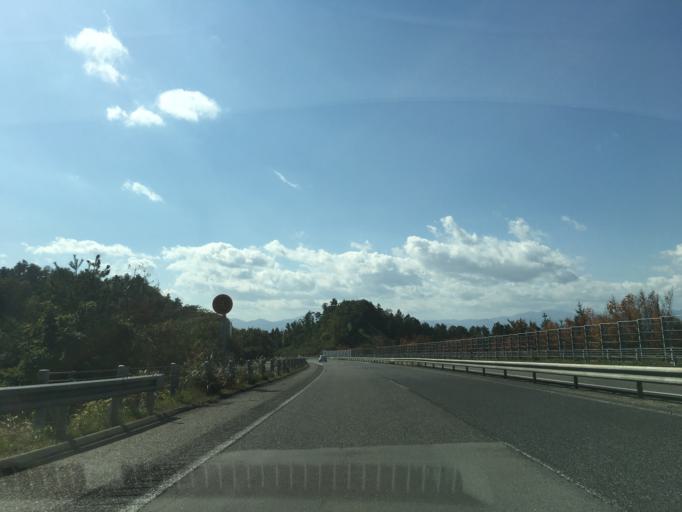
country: JP
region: Fukushima
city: Kitakata
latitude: 37.5448
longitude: 139.9581
